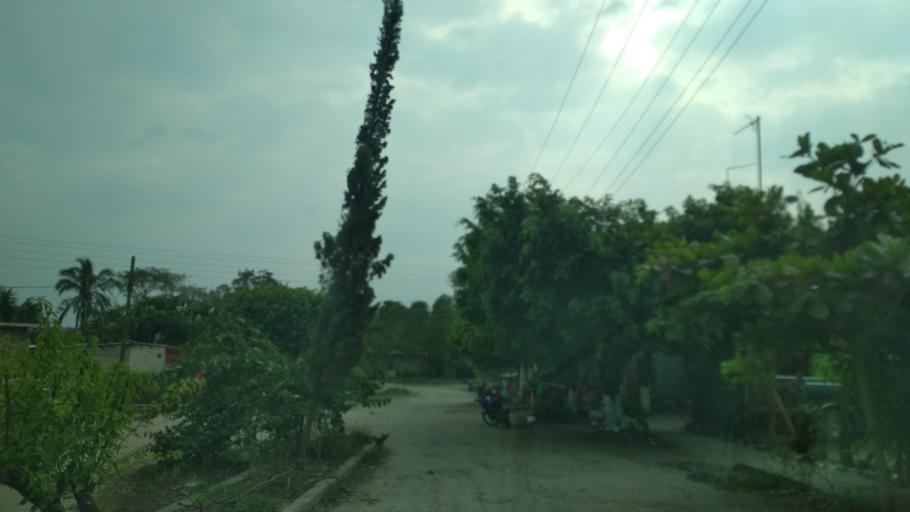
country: MM
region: Kayah
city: Loikaw
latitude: 20.2365
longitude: 97.2785
